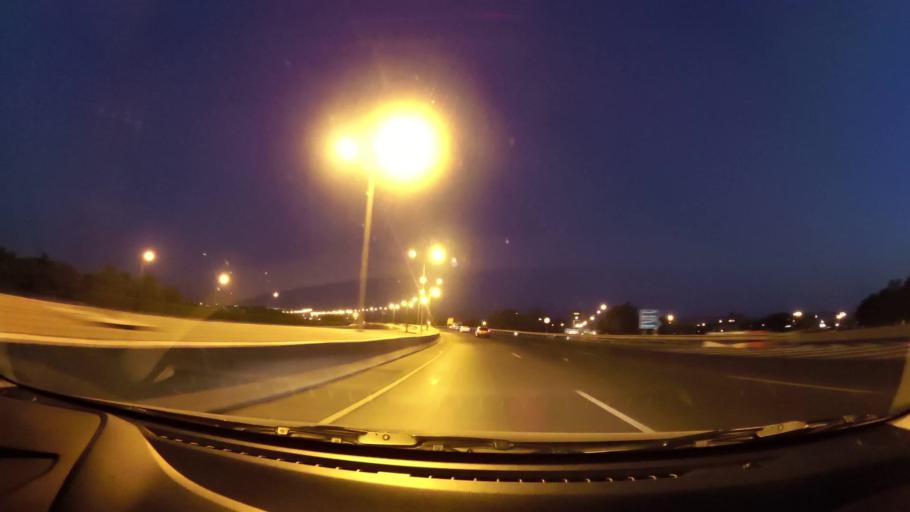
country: OM
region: Muhafazat Masqat
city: As Sib al Jadidah
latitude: 23.5921
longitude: 58.2512
